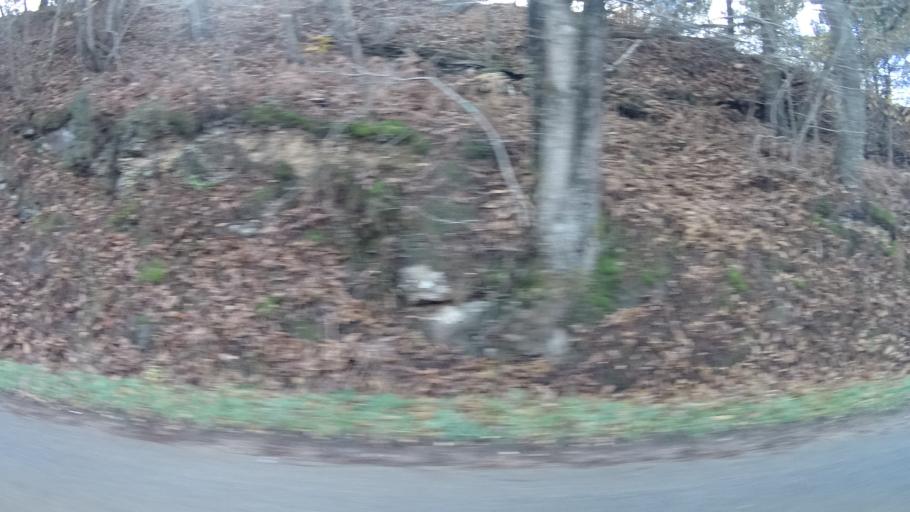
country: FR
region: Brittany
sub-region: Departement du Morbihan
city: Saint-Jean-la-Poterie
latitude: 47.6389
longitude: -2.1111
